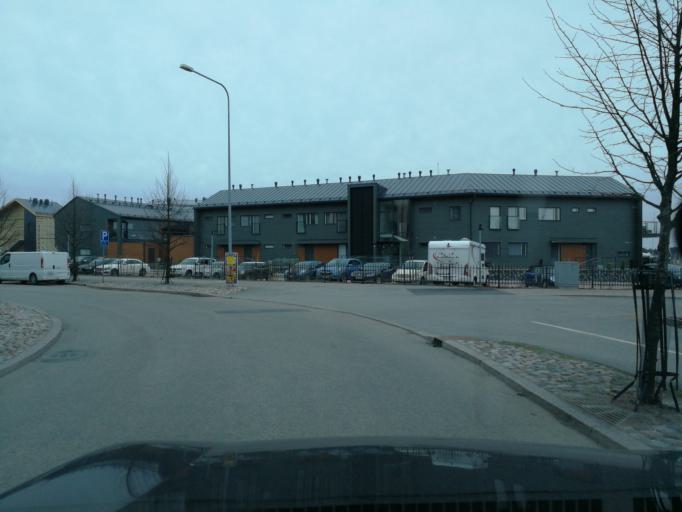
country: FI
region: Uusimaa
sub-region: Helsinki
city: Helsinki
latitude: 60.1894
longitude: 25.0260
